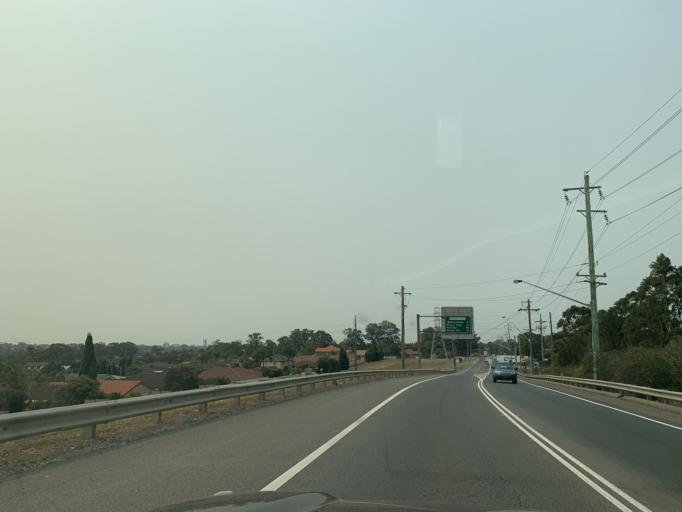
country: AU
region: New South Wales
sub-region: Holroyd
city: Girraween
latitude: -33.8014
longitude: 150.9163
